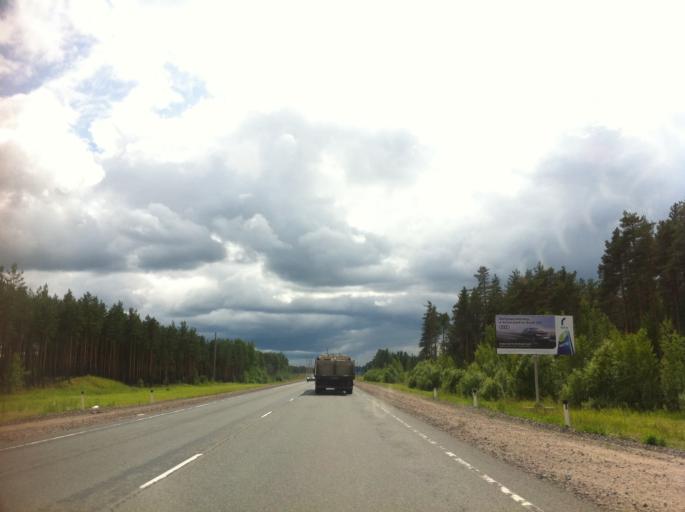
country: RU
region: Leningrad
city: Luga
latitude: 58.7387
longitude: 29.8891
